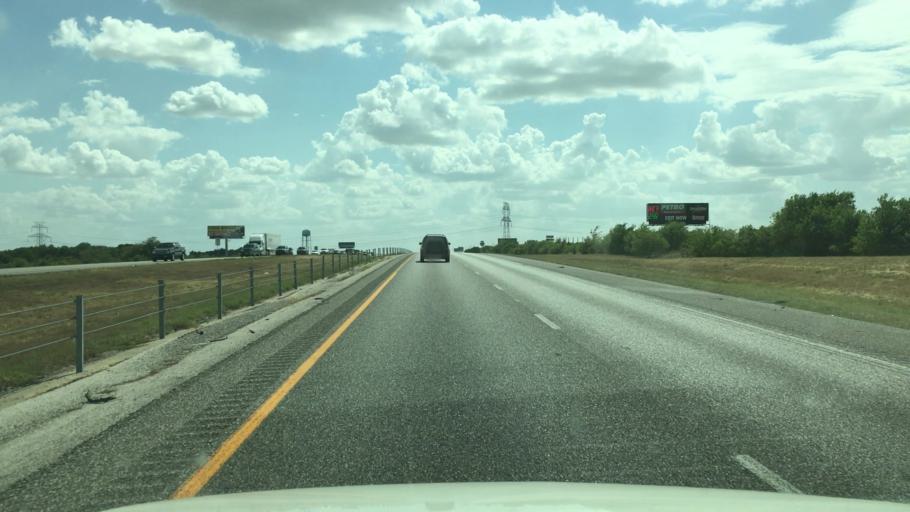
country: US
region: Texas
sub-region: Hill County
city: Hillsboro
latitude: 32.0847
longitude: -97.0420
